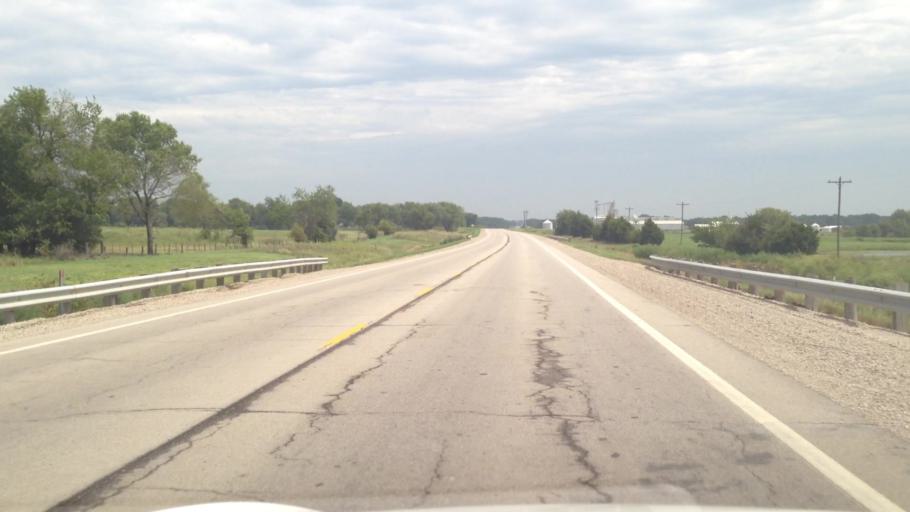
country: US
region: Kansas
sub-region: Crawford County
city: Girard
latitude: 37.5143
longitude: -94.9206
